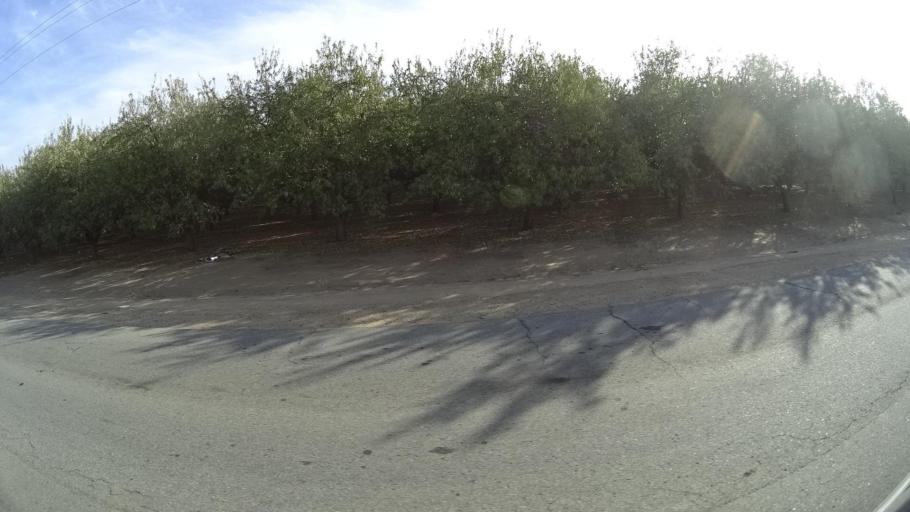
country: US
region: California
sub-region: Kern County
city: McFarland
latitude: 35.6543
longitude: -119.2046
